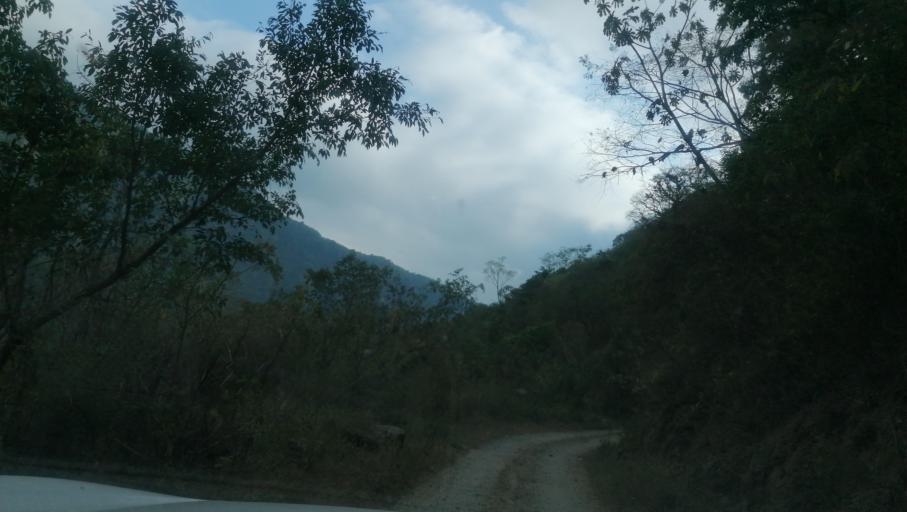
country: MX
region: Chiapas
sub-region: Cacahoatan
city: Benito Juarez
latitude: 15.1505
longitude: -92.1848
